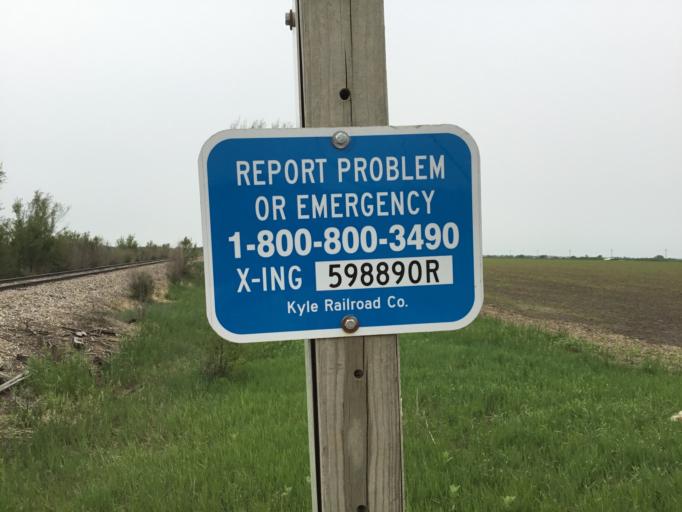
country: US
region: Kansas
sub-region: Republic County
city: Belleville
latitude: 39.7816
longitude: -97.8573
